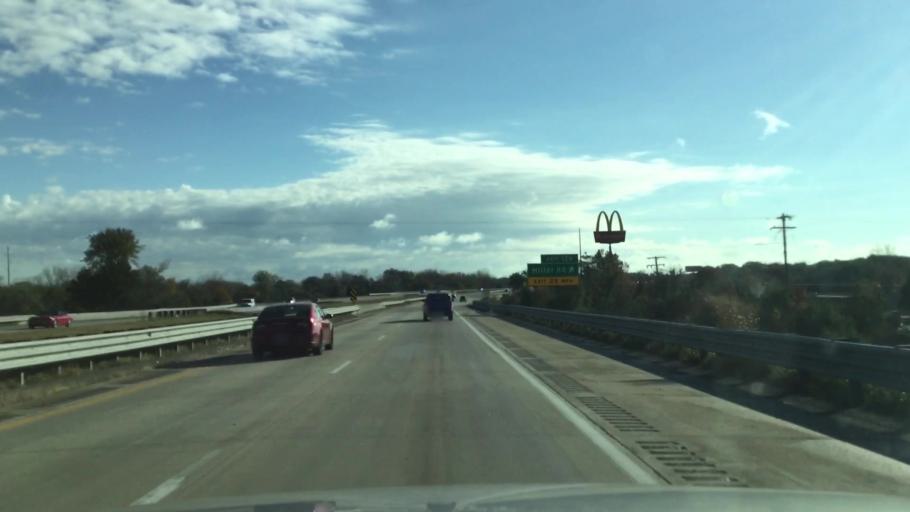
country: US
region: Michigan
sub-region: Genesee County
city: Swartz Creek
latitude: 42.9659
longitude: -83.8126
